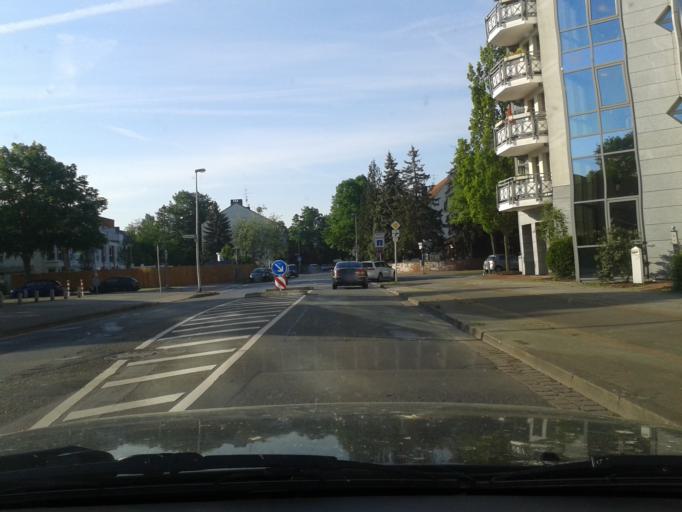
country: DE
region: Lower Saxony
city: Laatzen
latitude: 52.3357
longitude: 9.8000
